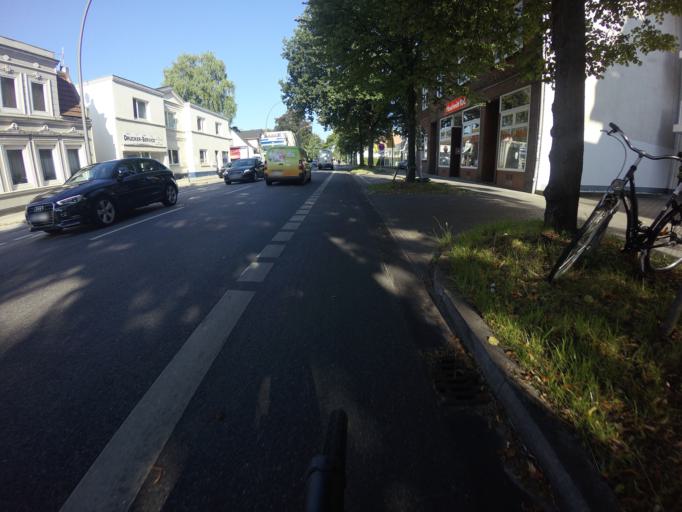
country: DE
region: Hamburg
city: Altona
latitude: 53.5677
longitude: 9.9062
